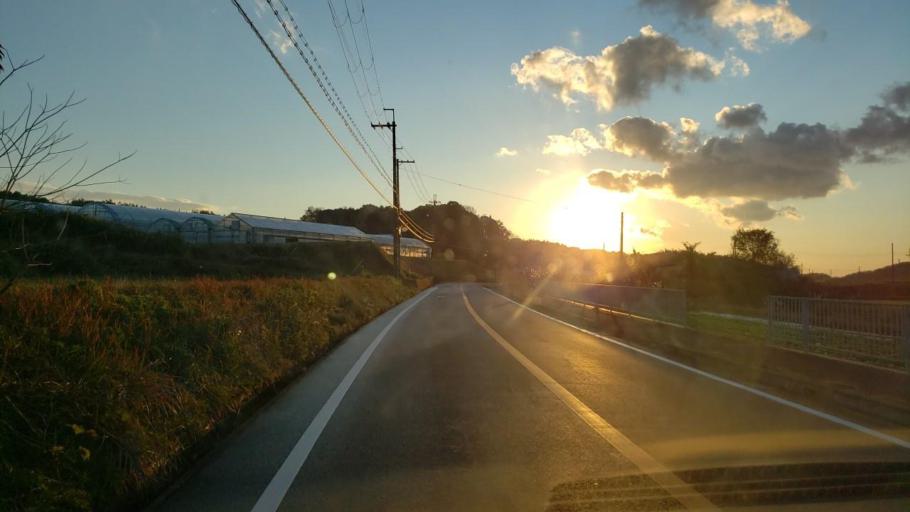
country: JP
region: Hyogo
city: Sumoto
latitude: 34.4021
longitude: 134.8315
